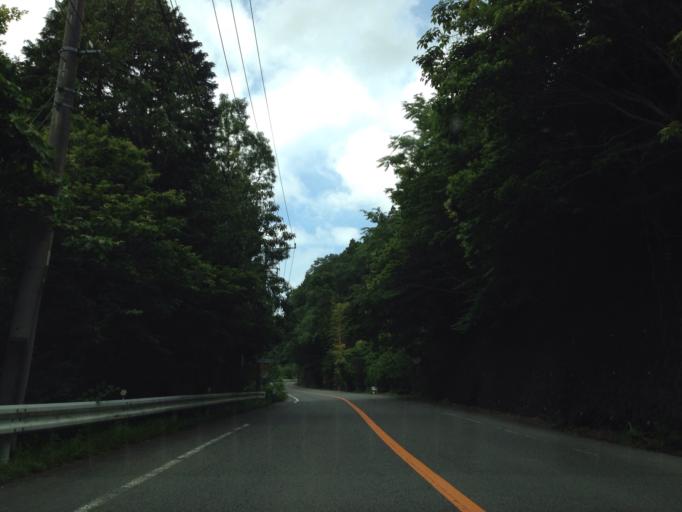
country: JP
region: Shizuoka
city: Heda
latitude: 34.9191
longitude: 138.8704
